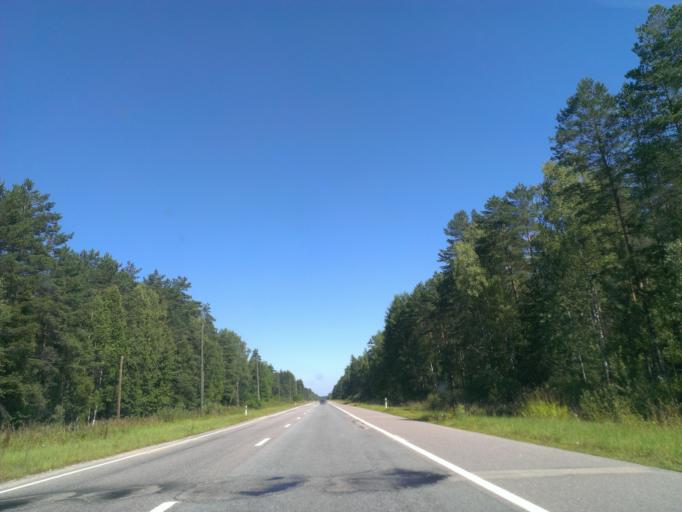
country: LV
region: Incukalns
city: Vangazi
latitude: 57.1023
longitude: 24.5928
